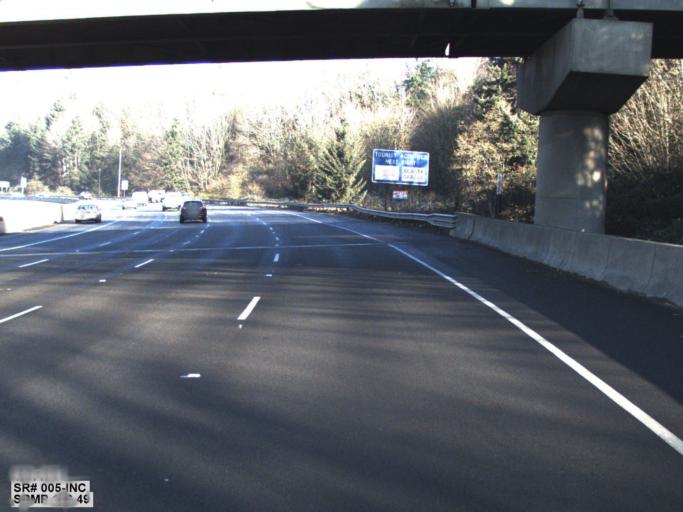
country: US
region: Washington
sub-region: King County
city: Tukwila
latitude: 47.4894
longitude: -122.2643
